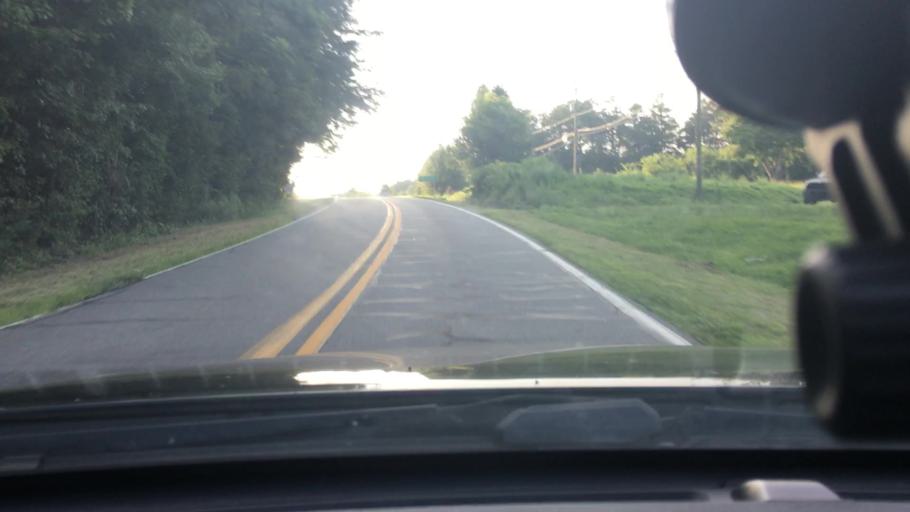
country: US
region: North Carolina
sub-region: McDowell County
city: West Marion
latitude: 35.6317
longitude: -81.9992
